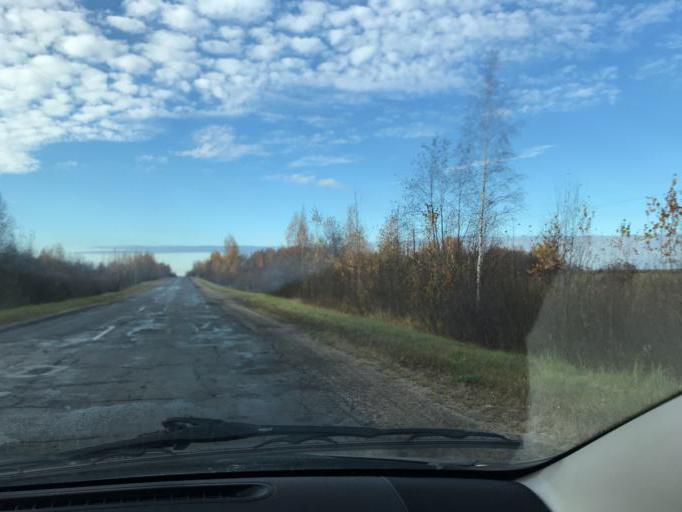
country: BY
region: Vitebsk
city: Haradok
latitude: 55.4185
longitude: 29.7829
